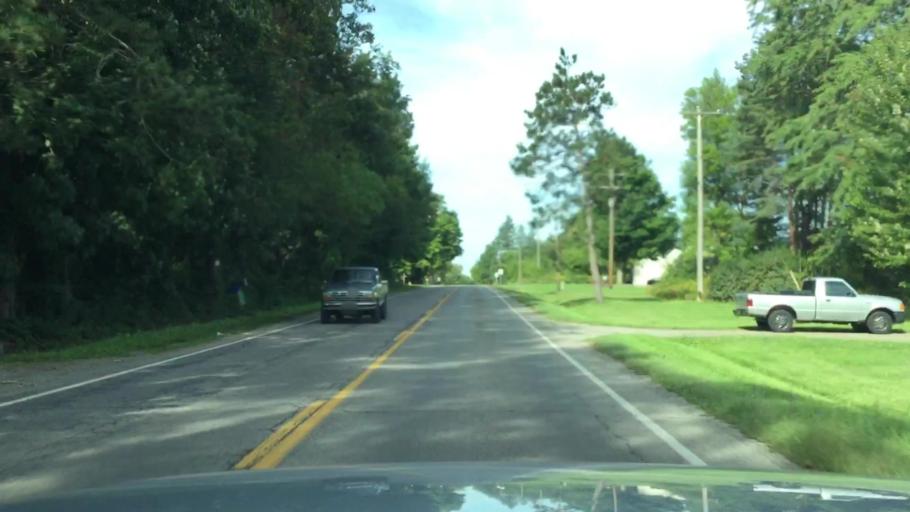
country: US
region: Michigan
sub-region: Genesee County
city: Montrose
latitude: 43.1178
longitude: -83.8789
